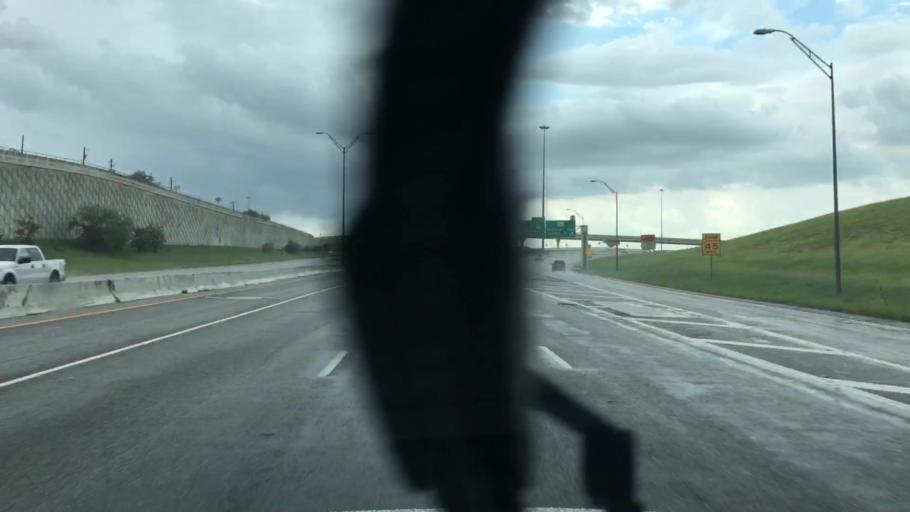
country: US
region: Texas
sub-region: Nueces County
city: Robstown
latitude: 27.8619
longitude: -97.6173
